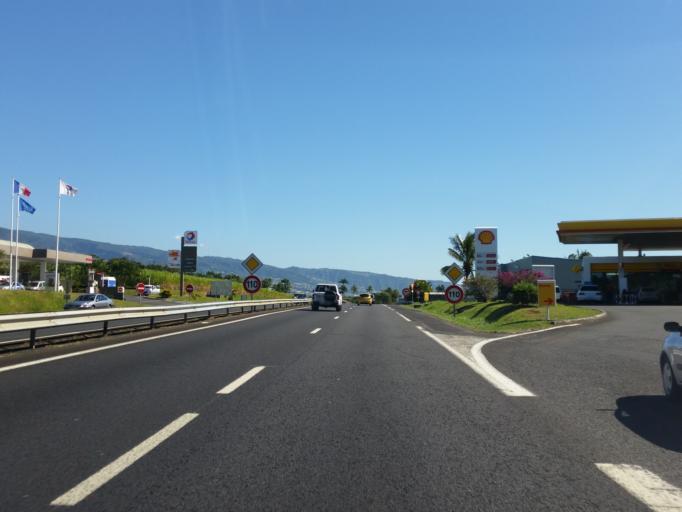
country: RE
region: Reunion
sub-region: Reunion
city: Sainte-Marie
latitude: -20.8979
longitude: 55.5688
